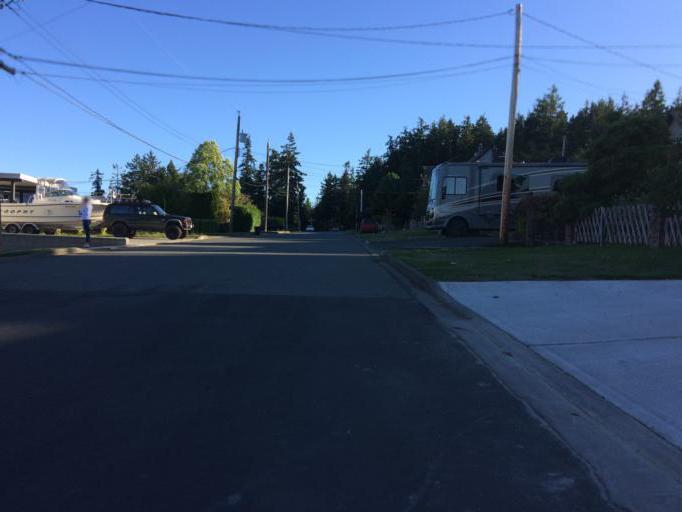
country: CA
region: British Columbia
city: Campbell River
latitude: 50.0174
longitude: -125.2380
